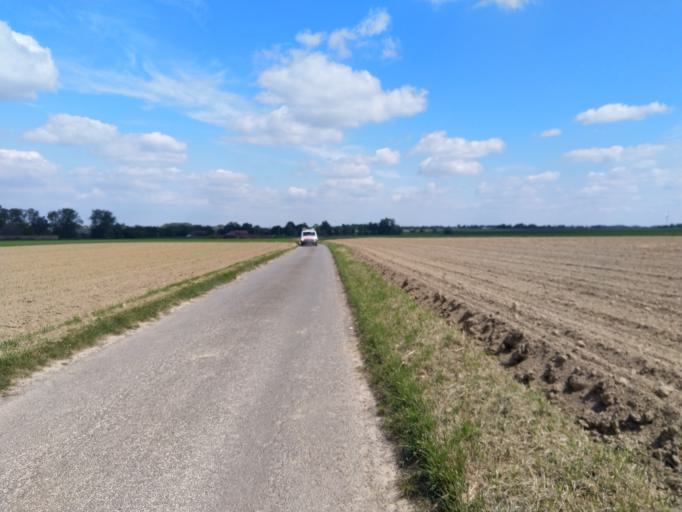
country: BE
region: Wallonia
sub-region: Province du Hainaut
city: Soignies
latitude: 50.5851
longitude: 4.0250
